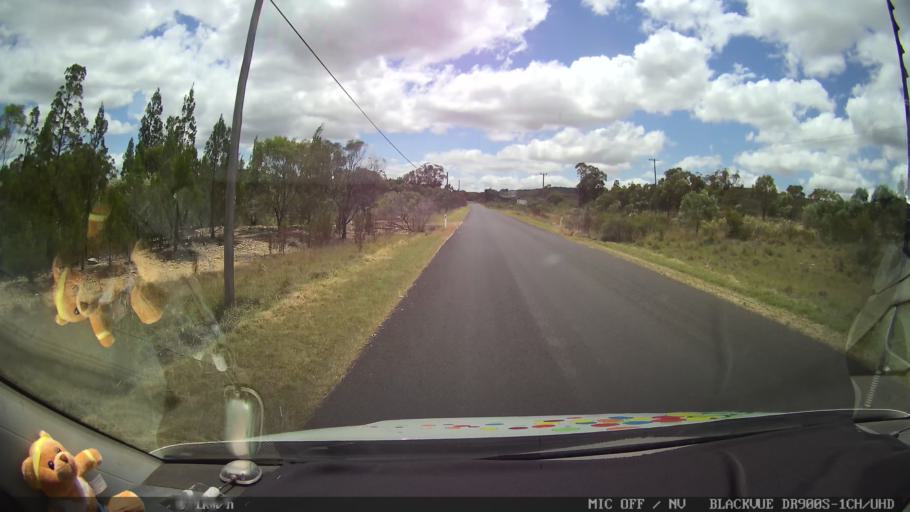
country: AU
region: New South Wales
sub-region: Glen Innes Severn
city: Glen Innes
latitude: -29.4430
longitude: 151.6053
